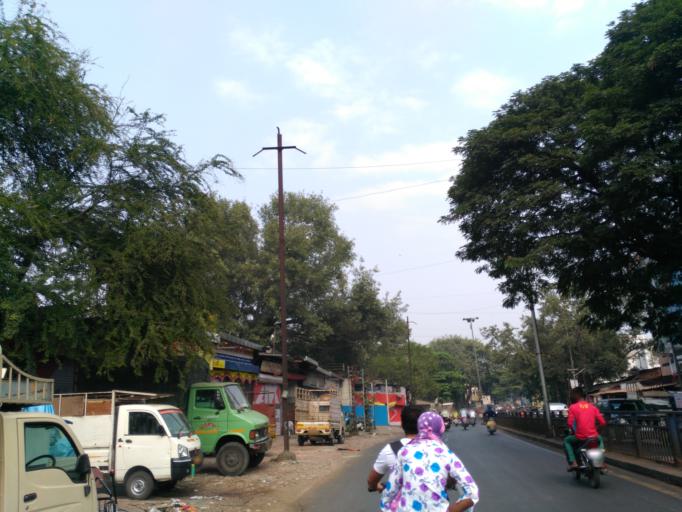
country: IN
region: Maharashtra
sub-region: Pune Division
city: Pune
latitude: 18.5093
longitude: 73.8684
